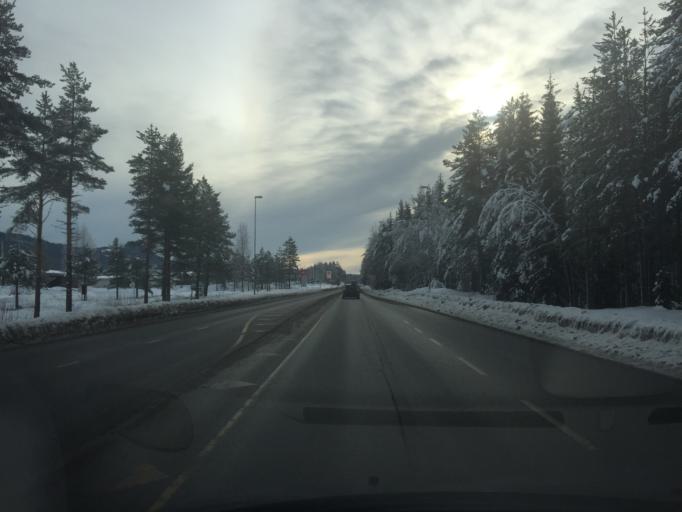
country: NO
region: Hedmark
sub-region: Trysil
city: Innbygda
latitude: 61.2966
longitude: 12.2675
